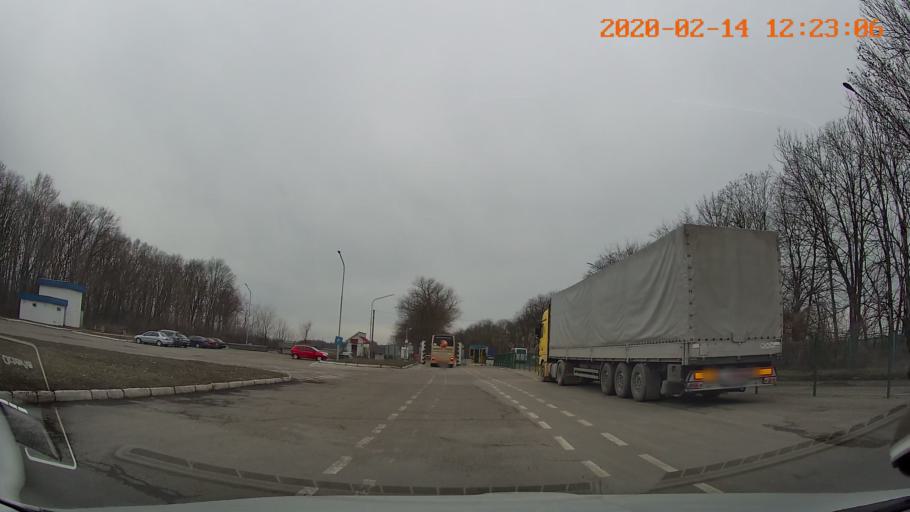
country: RO
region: Botosani
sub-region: Comuna Paltinis
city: Paltinis
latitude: 48.2643
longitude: 26.6215
